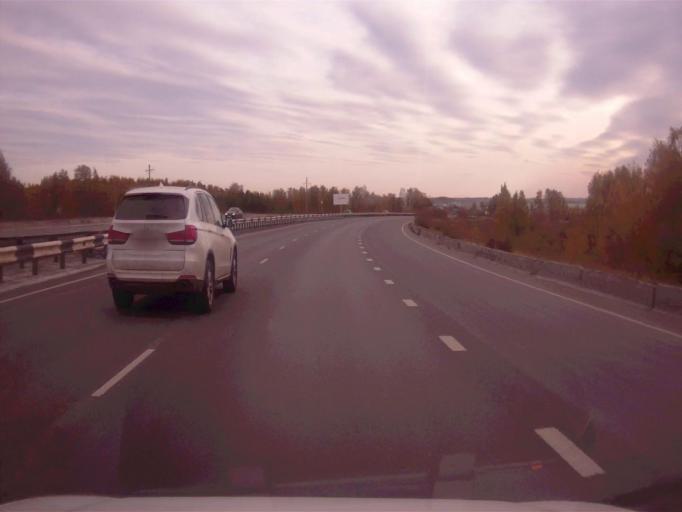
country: RU
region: Chelyabinsk
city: Novosineglazovskiy
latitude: 55.0391
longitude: 61.4404
